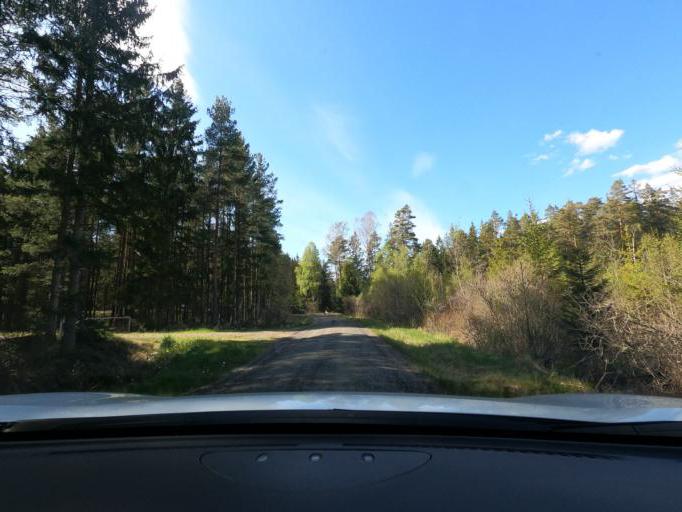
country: SE
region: Vaestra Goetaland
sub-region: Harryda Kommun
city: Ravlanda
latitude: 57.5937
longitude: 12.4817
